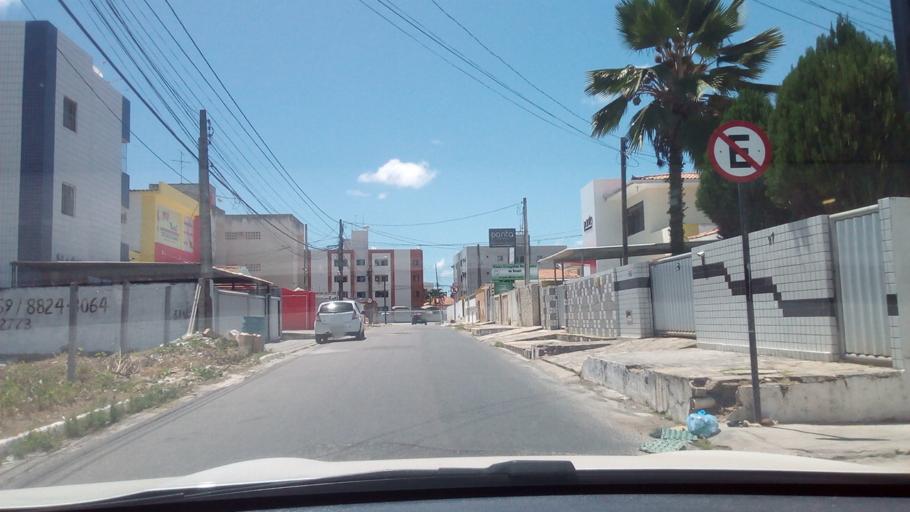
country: BR
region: Paraiba
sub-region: Joao Pessoa
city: Joao Pessoa
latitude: -7.1508
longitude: -34.8370
